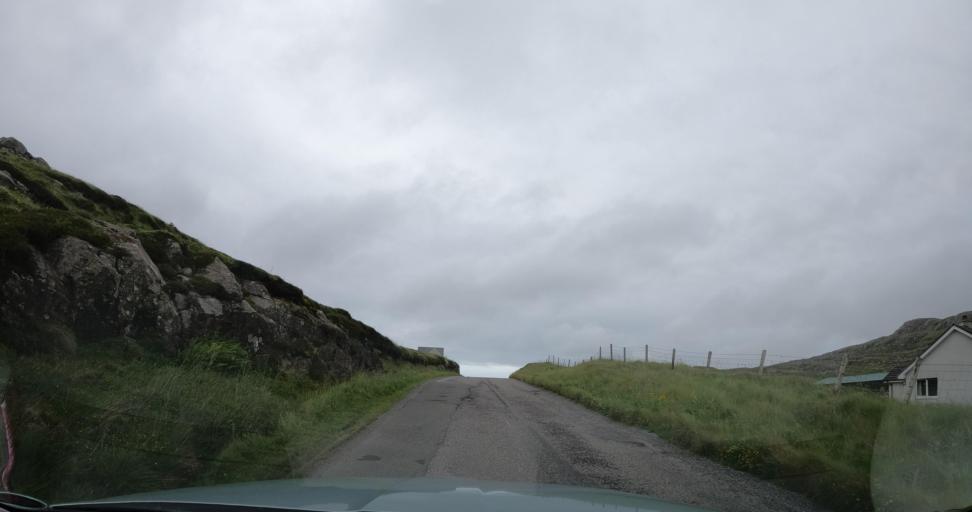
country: GB
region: Scotland
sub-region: Eilean Siar
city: Barra
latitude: 56.9617
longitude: -7.5078
